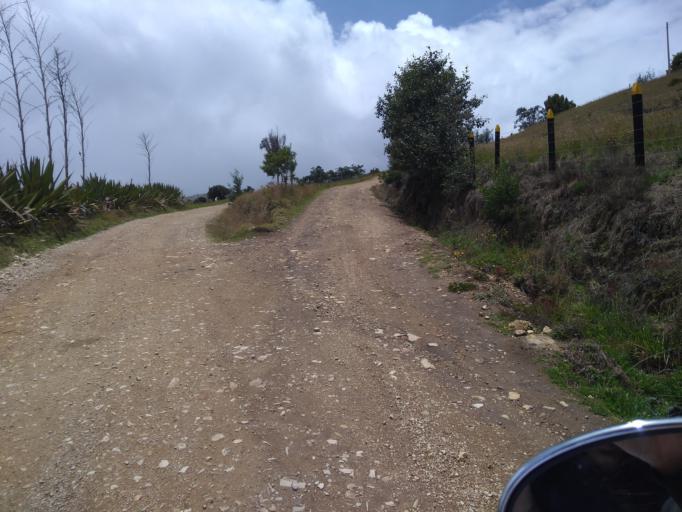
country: CO
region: Boyaca
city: Toca
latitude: 5.5777
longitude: -73.1482
